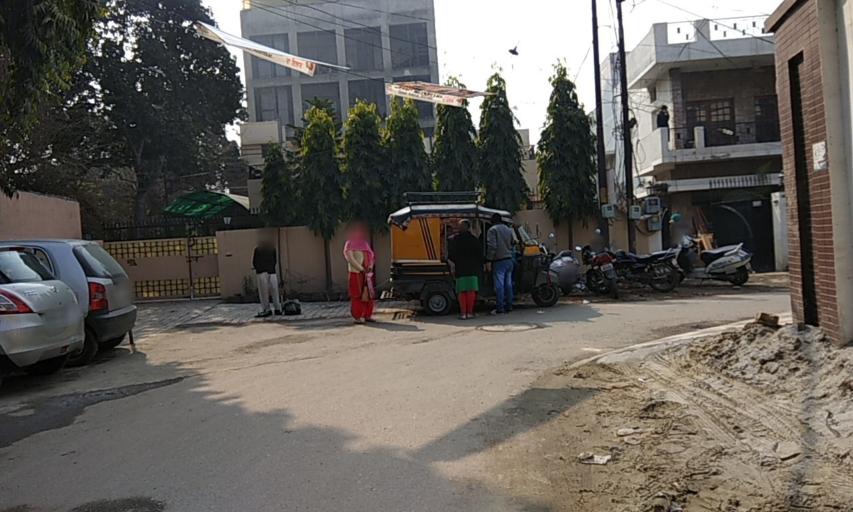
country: IN
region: Punjab
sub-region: Amritsar
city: Amritsar
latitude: 31.6435
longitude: 74.8664
